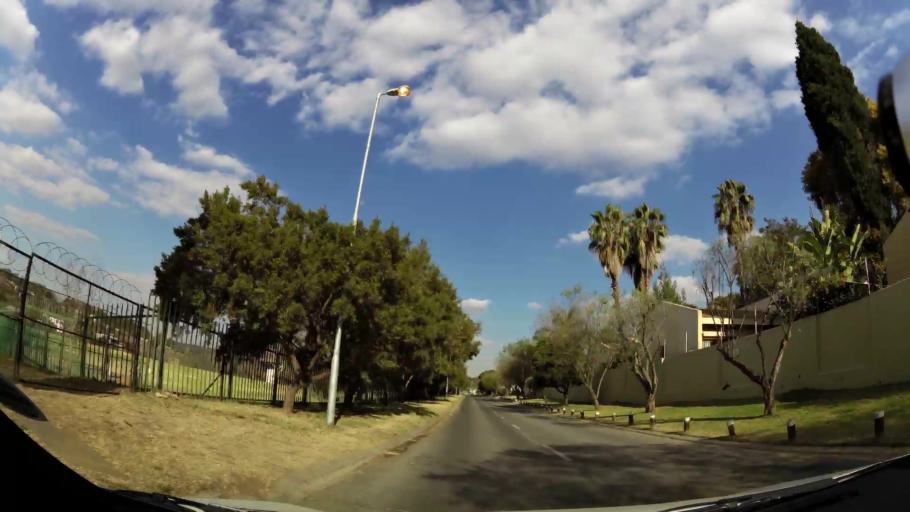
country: ZA
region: Gauteng
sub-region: City of Johannesburg Metropolitan Municipality
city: Diepsloot
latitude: -26.0064
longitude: 28.0313
